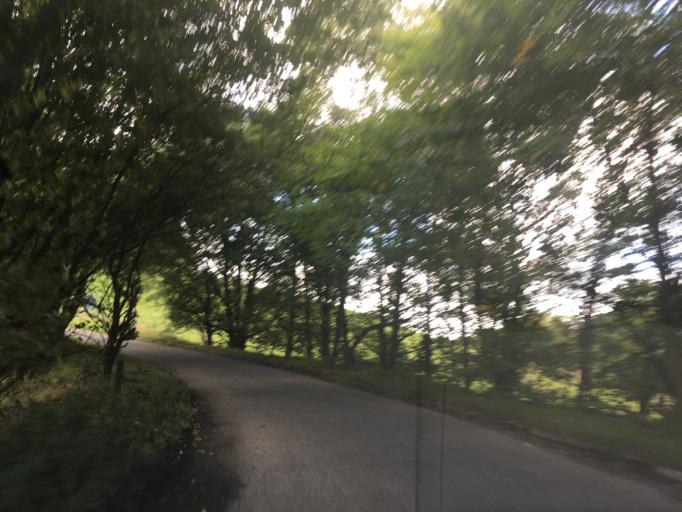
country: GB
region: Scotland
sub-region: Edinburgh
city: Queensferry
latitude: 55.9789
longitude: -3.3473
